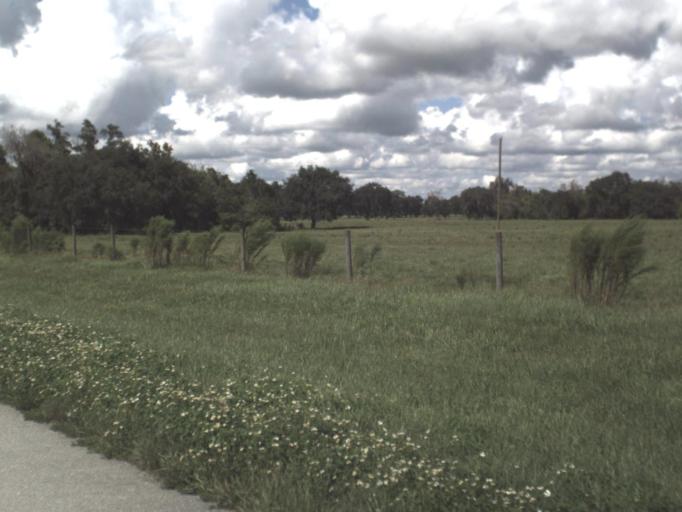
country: US
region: Florida
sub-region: DeSoto County
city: Arcadia
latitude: 27.2496
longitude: -81.9553
